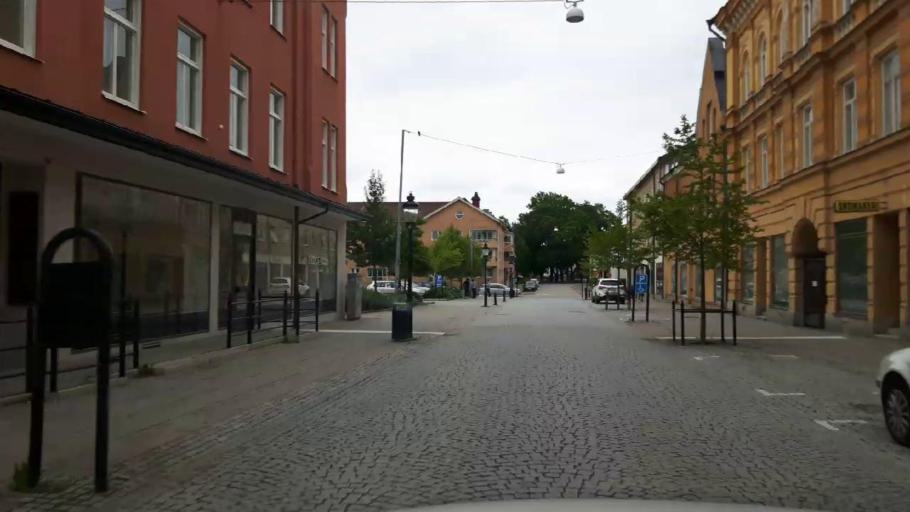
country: SE
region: Vaestmanland
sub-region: Kopings Kommun
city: Koping
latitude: 59.5125
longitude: 15.9949
